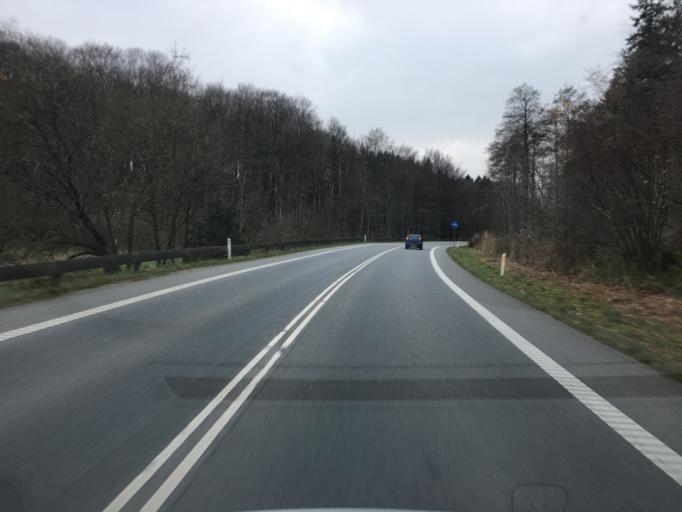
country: DK
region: South Denmark
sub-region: Aabenraa Kommune
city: Aabenraa
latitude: 55.0288
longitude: 9.3763
